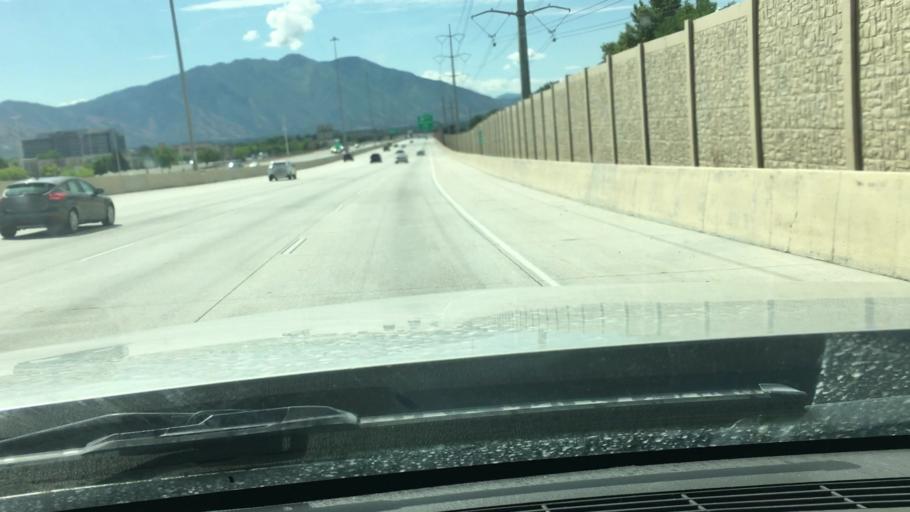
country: US
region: Utah
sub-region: Utah County
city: Provo
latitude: 40.2165
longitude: -111.6660
